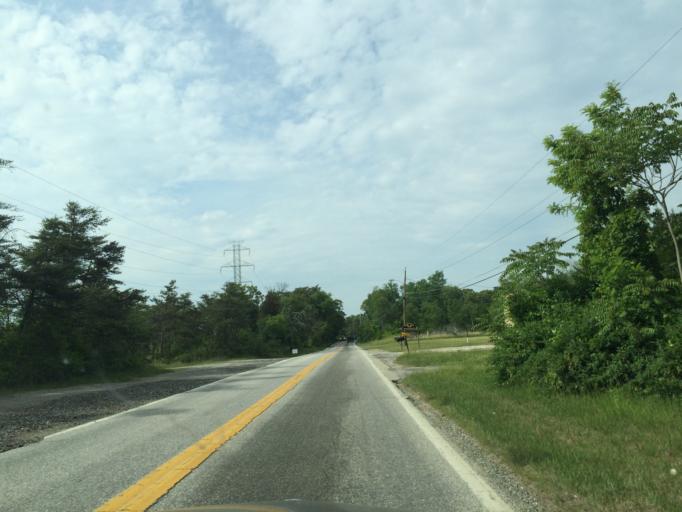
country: US
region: Maryland
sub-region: Baltimore County
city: Reisterstown
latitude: 39.4206
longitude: -76.8404
